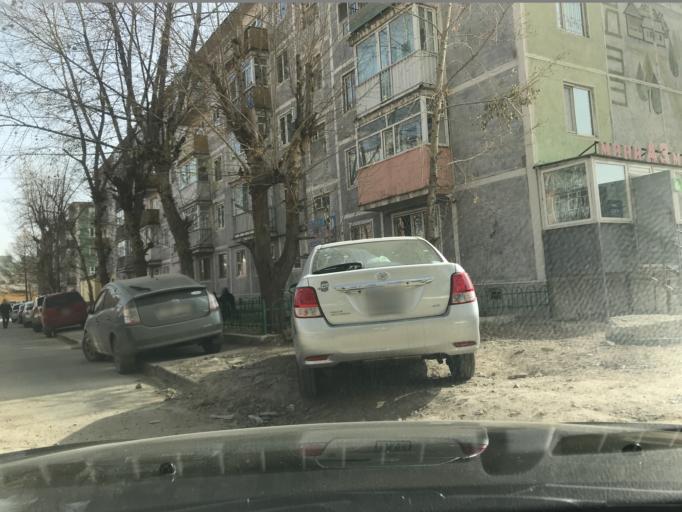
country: MN
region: Ulaanbaatar
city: Ulaanbaatar
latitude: 47.9187
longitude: 106.9484
